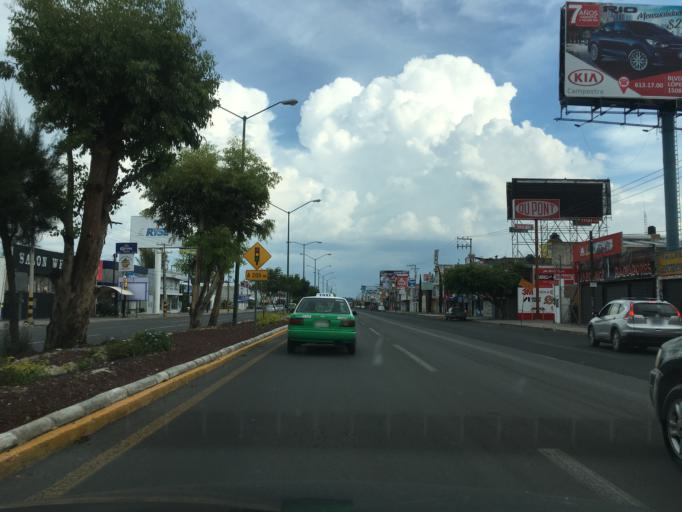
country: MX
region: Guanajuato
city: Celaya
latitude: 20.5424
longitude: -100.8208
